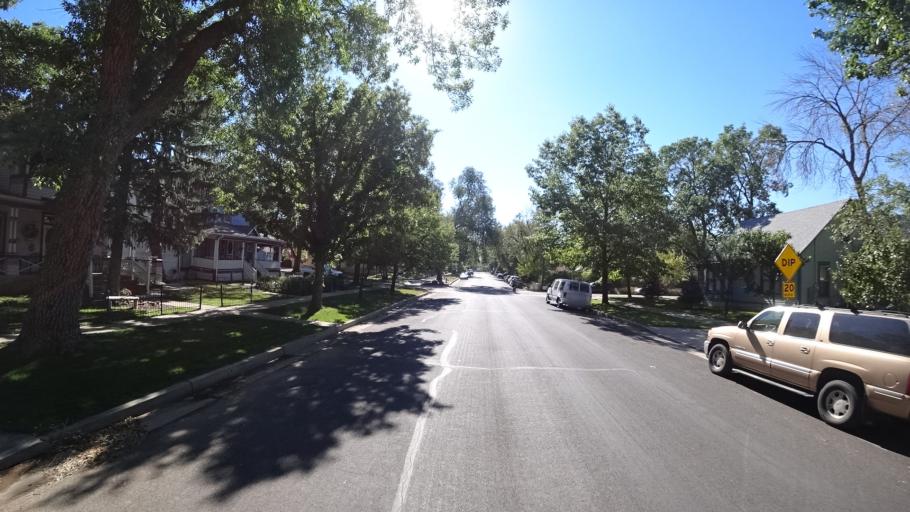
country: US
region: Colorado
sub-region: El Paso County
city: Colorado Springs
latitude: 38.8368
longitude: -104.8425
